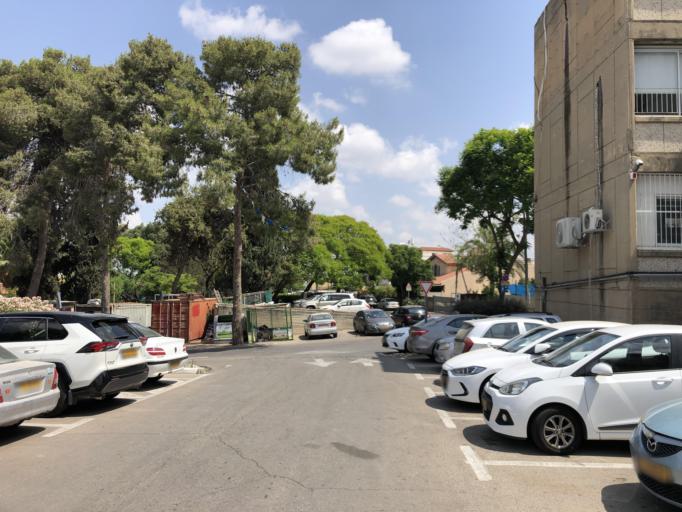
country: IL
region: Central District
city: Rosh Ha'Ayin
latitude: 32.0937
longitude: 34.9570
